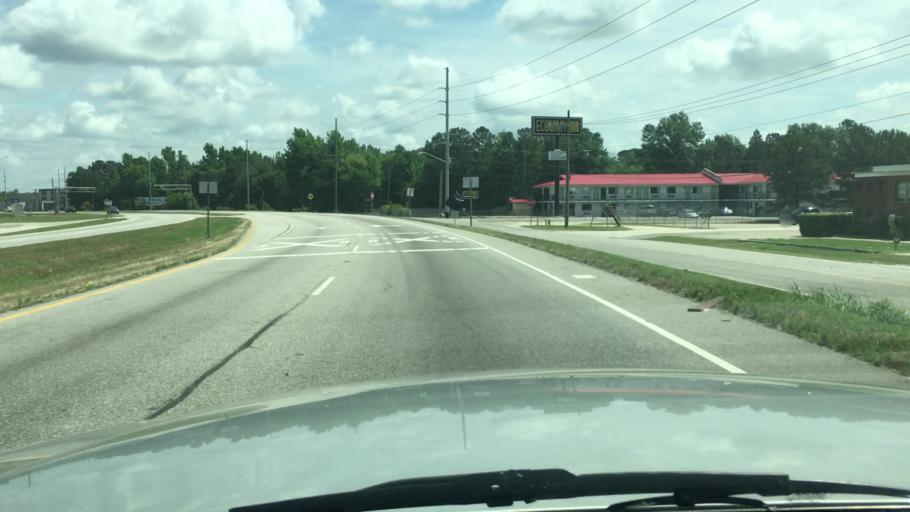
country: US
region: North Carolina
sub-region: Cumberland County
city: Fayetteville
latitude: 35.0374
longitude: -78.8679
